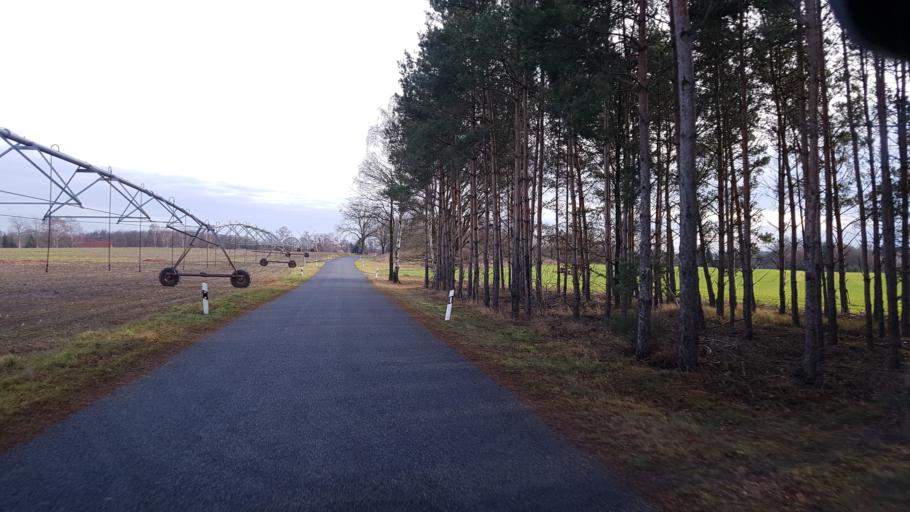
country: DE
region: Brandenburg
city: Bronkow
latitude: 51.6549
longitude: 13.8916
